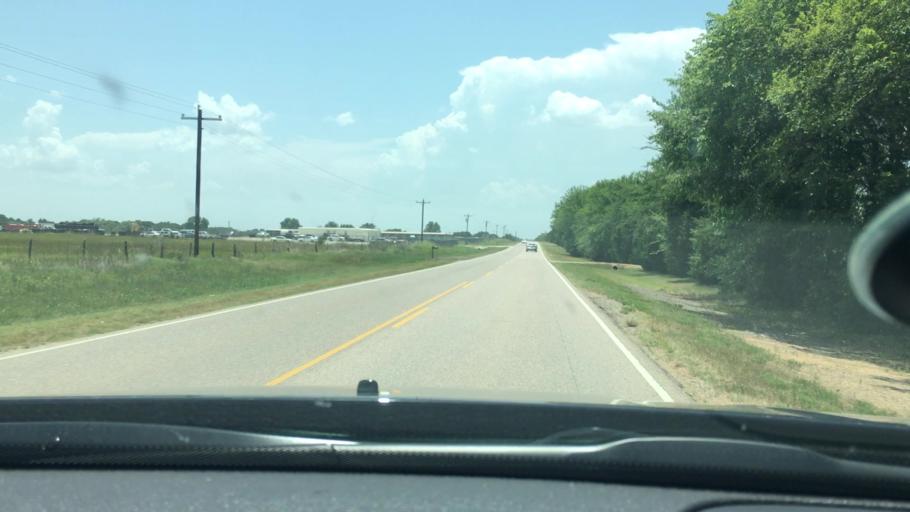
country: US
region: Oklahoma
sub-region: Johnston County
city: Tishomingo
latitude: 34.2848
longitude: -96.6711
